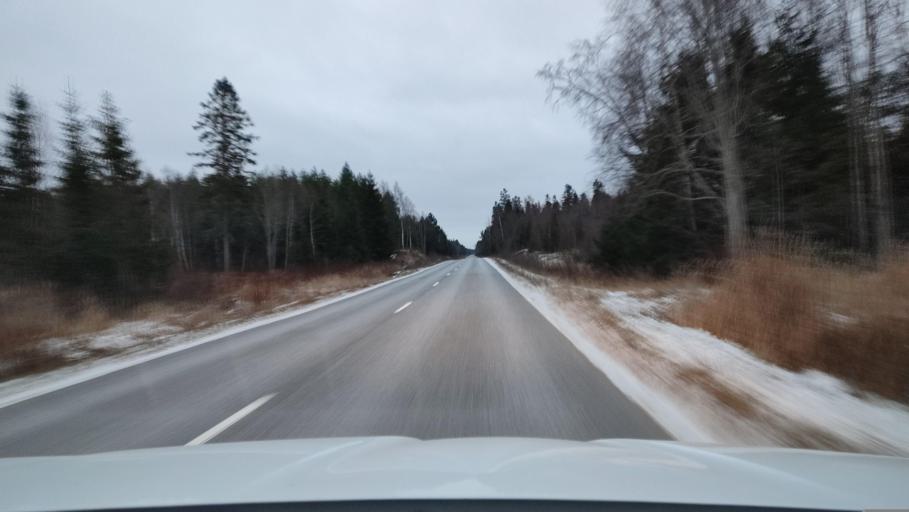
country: FI
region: Ostrobothnia
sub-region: Vaasa
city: Replot
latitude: 63.2580
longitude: 21.3654
